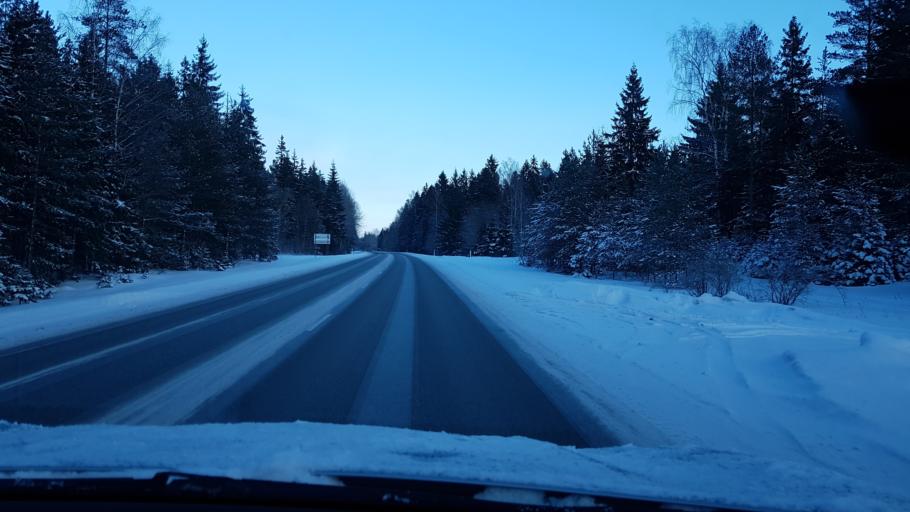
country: EE
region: Harju
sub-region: Nissi vald
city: Riisipere
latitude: 59.1796
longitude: 24.3769
